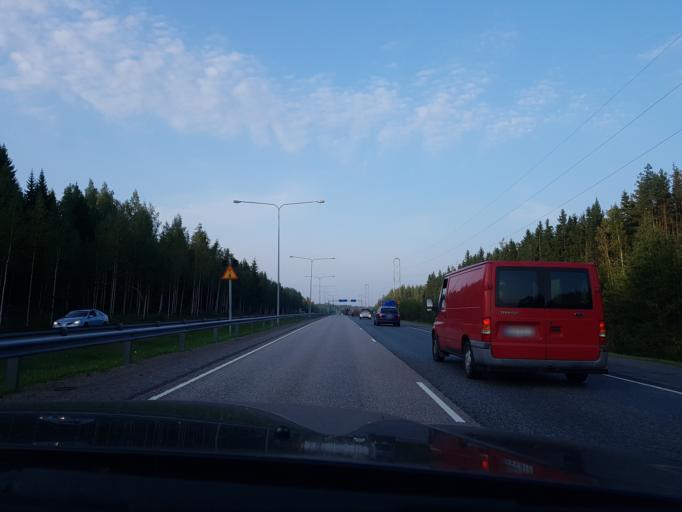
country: FI
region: Uusimaa
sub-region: Helsinki
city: Tuusula
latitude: 60.3630
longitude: 25.0043
